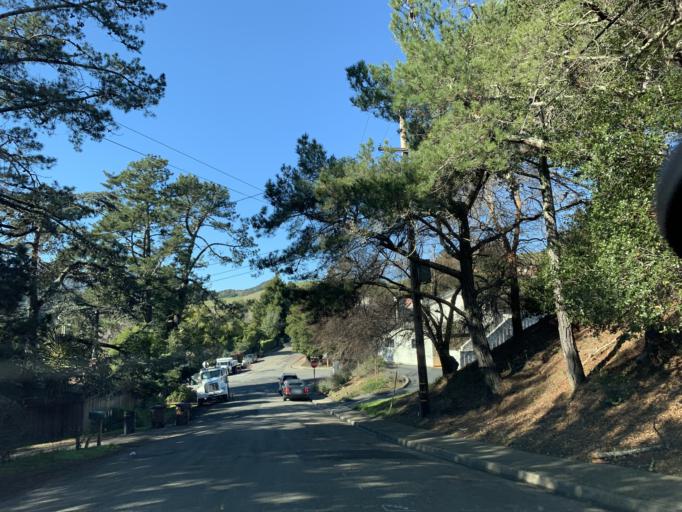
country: US
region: California
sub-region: Marin County
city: Strawberry
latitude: 37.9057
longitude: -122.5128
